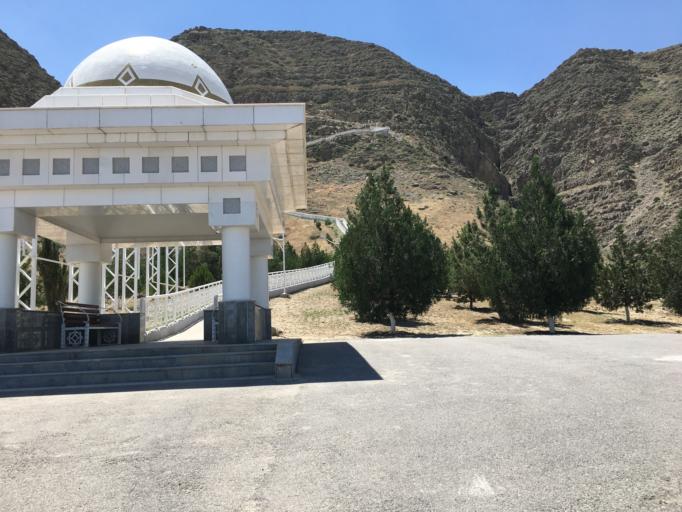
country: TM
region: Ahal
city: Arcabil
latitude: 37.9358
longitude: 58.2062
